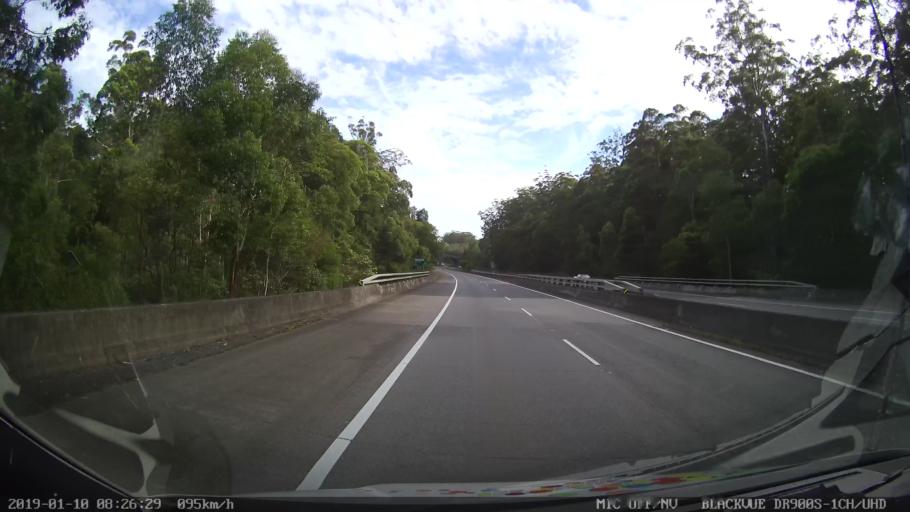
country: AU
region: New South Wales
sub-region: Coffs Harbour
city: Bonville
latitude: -30.4204
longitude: 153.0240
